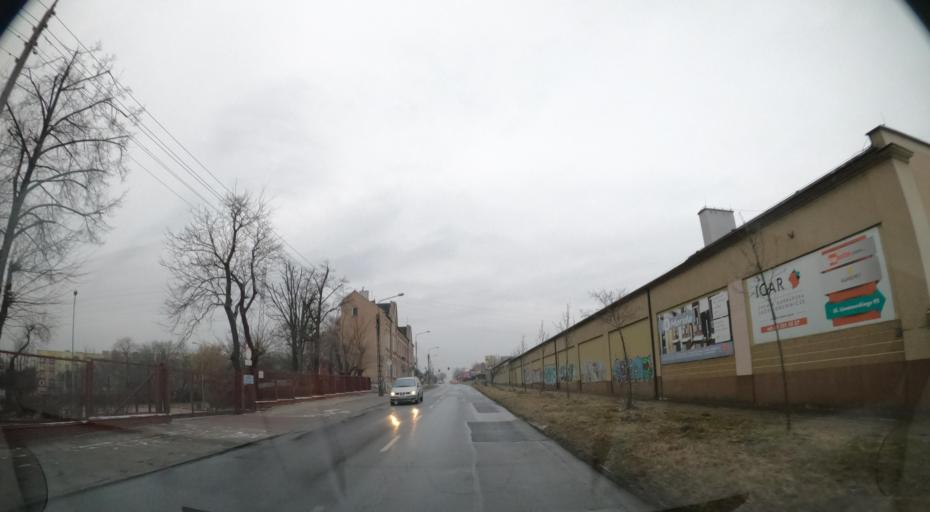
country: PL
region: Masovian Voivodeship
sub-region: Radom
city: Radom
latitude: 51.3844
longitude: 21.1230
